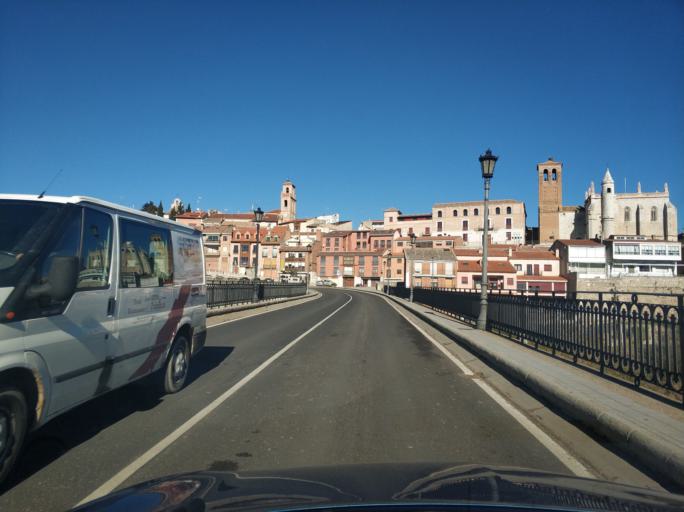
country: ES
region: Castille and Leon
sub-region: Provincia de Valladolid
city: Tordesillas
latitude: 41.4983
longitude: -5.0009
